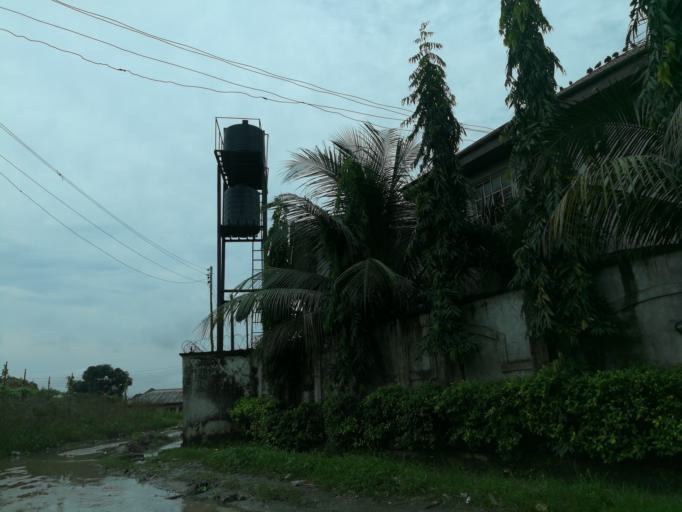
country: NG
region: Rivers
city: Port Harcourt
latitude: 4.8600
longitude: 7.0366
